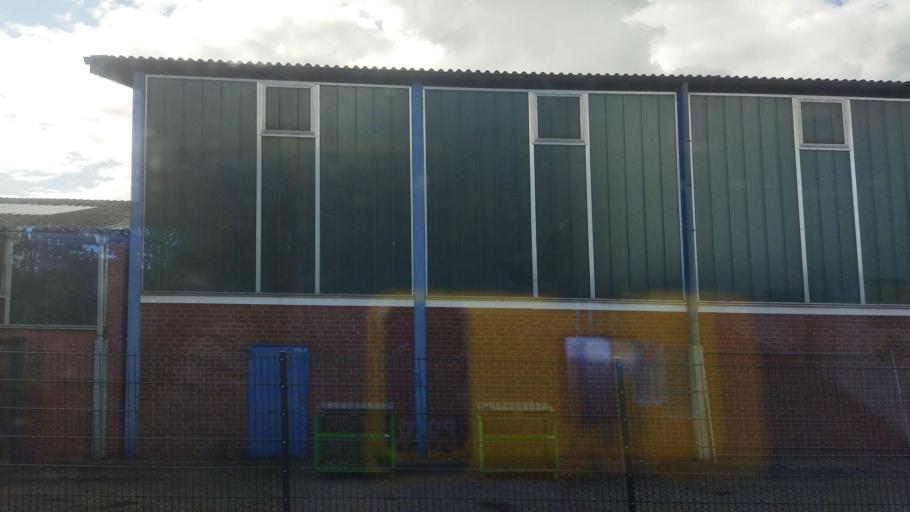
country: DE
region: Lower Saxony
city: Emsburen
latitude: 52.3928
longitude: 7.3087
